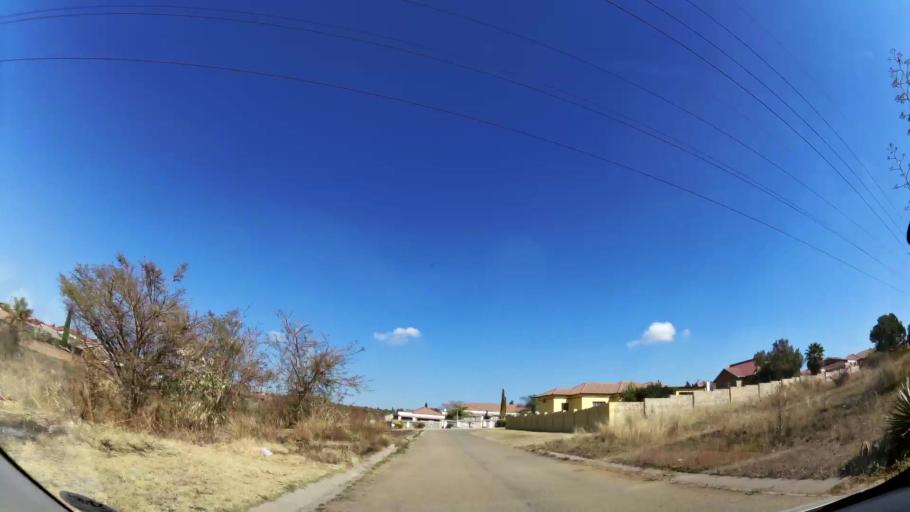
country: ZA
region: Mpumalanga
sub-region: Nkangala District Municipality
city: Witbank
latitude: -25.8586
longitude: 29.2459
